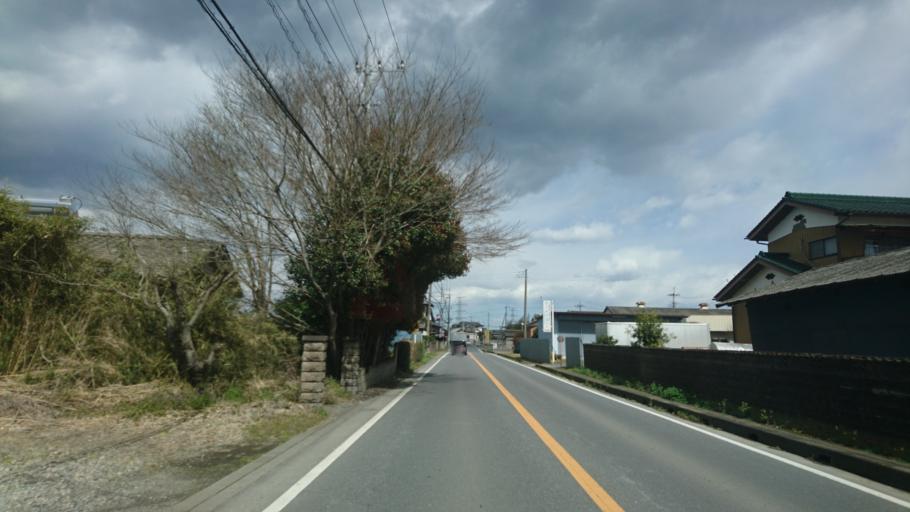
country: JP
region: Ibaraki
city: Yuki
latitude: 36.2607
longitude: 139.9144
